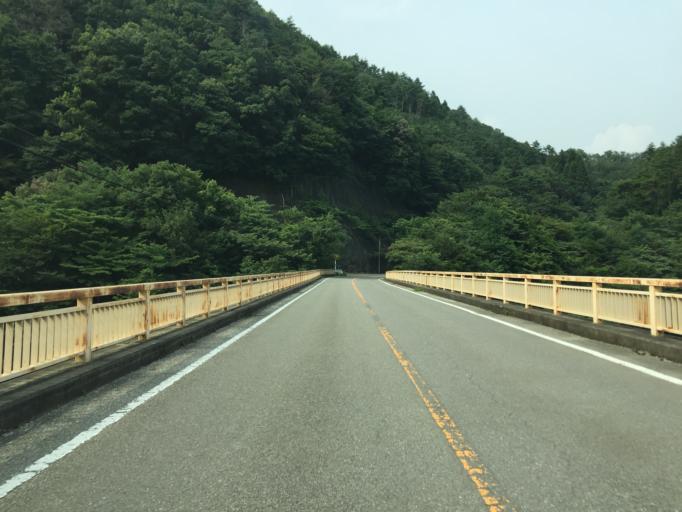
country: JP
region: Fukushima
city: Namie
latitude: 37.5949
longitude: 140.8951
